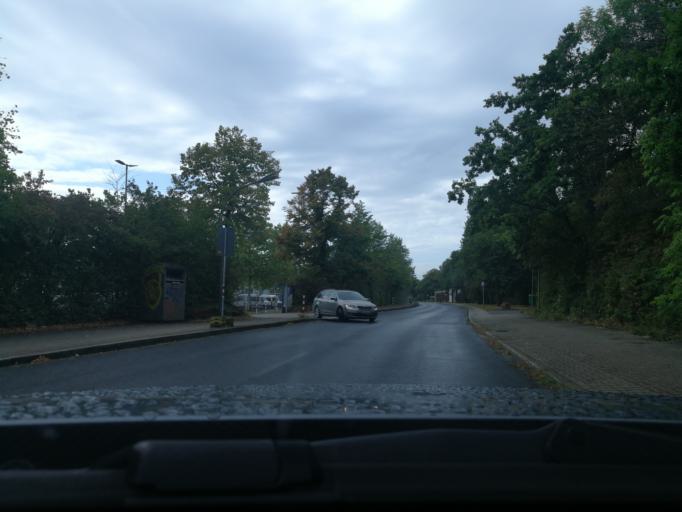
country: DE
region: North Rhine-Westphalia
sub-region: Regierungsbezirk Dusseldorf
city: Dusseldorf
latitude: 51.2631
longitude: 6.7881
